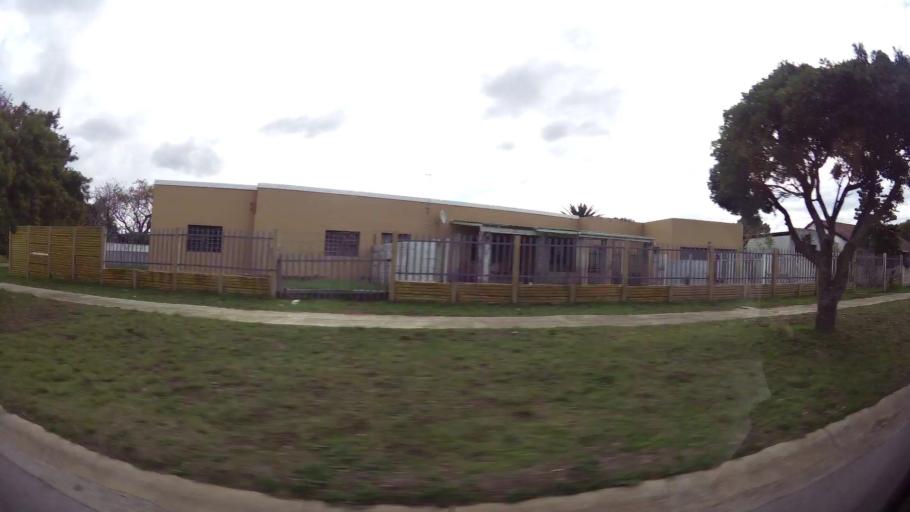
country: ZA
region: Eastern Cape
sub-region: Nelson Mandela Bay Metropolitan Municipality
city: Port Elizabeth
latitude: -33.9387
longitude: 25.5220
